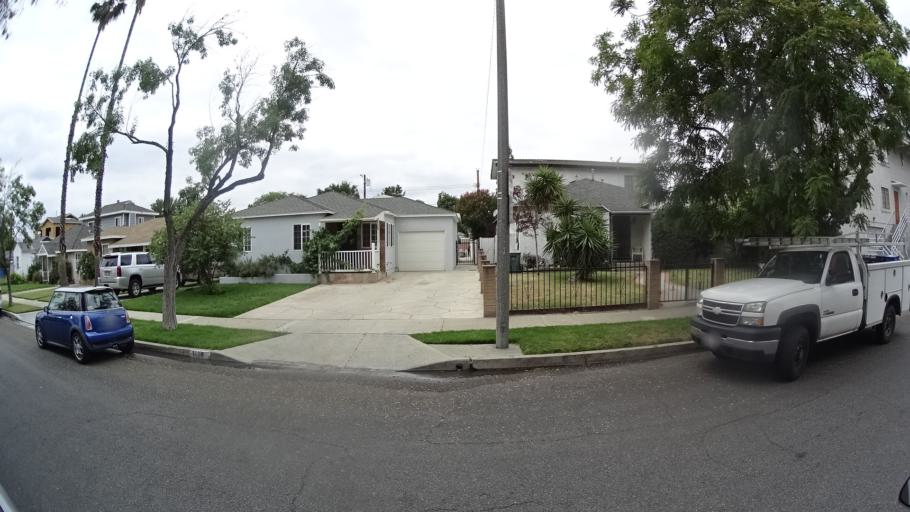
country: US
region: California
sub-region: Los Angeles County
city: Burbank
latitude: 34.1838
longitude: -118.3276
